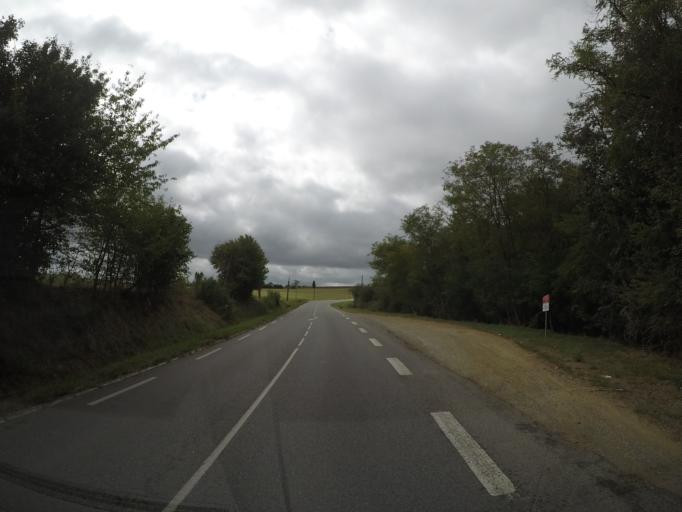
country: FR
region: Midi-Pyrenees
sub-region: Departement de la Haute-Garonne
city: Saint-Sulpice-sur-Leze
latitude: 43.3342
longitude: 1.3105
